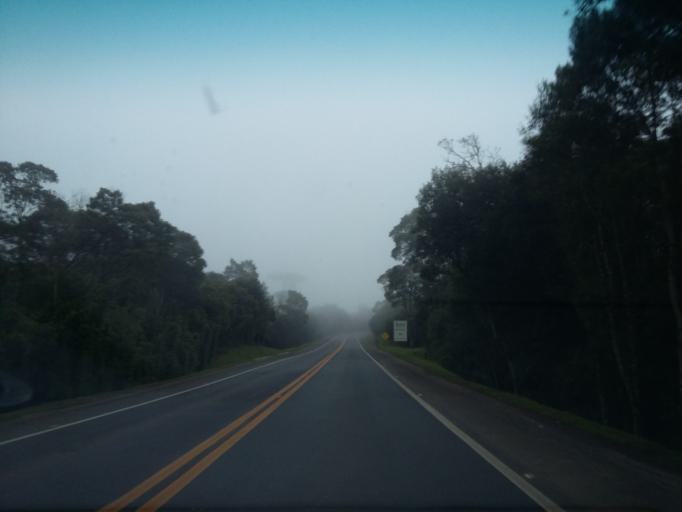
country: BR
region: Santa Catarina
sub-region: Curitibanos
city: Curitibanos
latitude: -27.2950
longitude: -50.4305
